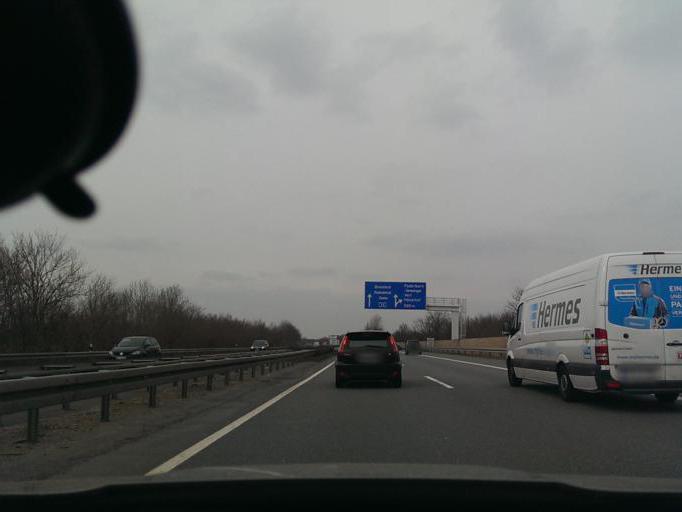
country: DE
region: North Rhine-Westphalia
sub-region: Regierungsbezirk Detmold
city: Hovelhof
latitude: 51.7798
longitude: 8.7030
